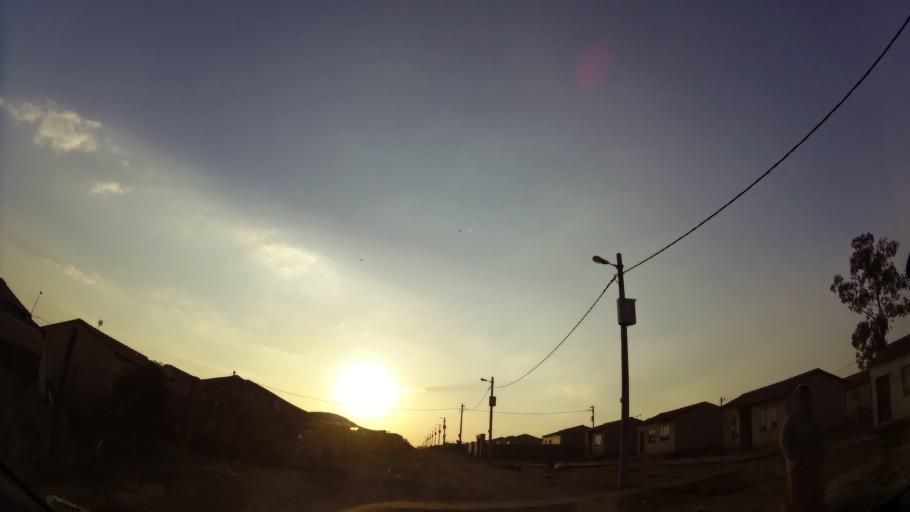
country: ZA
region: Gauteng
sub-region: Ekurhuleni Metropolitan Municipality
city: Benoni
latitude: -26.1643
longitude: 28.3788
